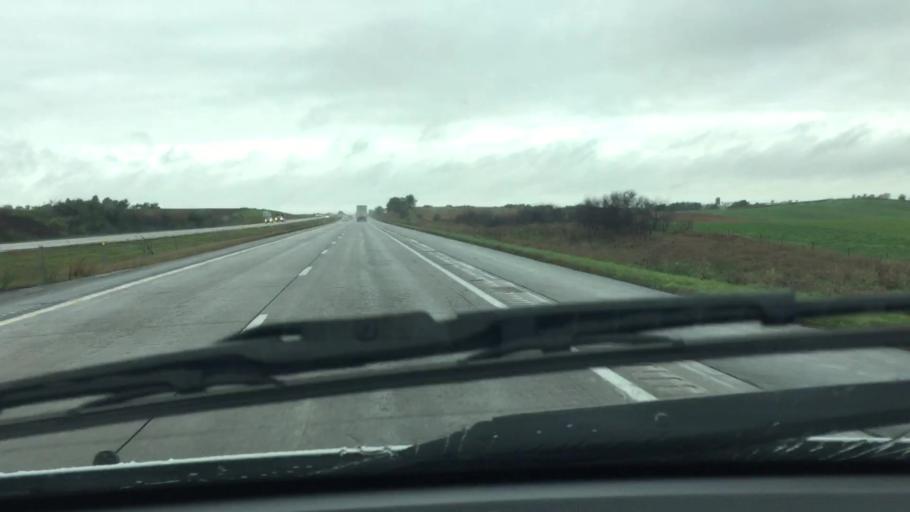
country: US
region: Iowa
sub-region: Poweshiek County
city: Brooklyn
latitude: 41.6952
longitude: -92.4648
